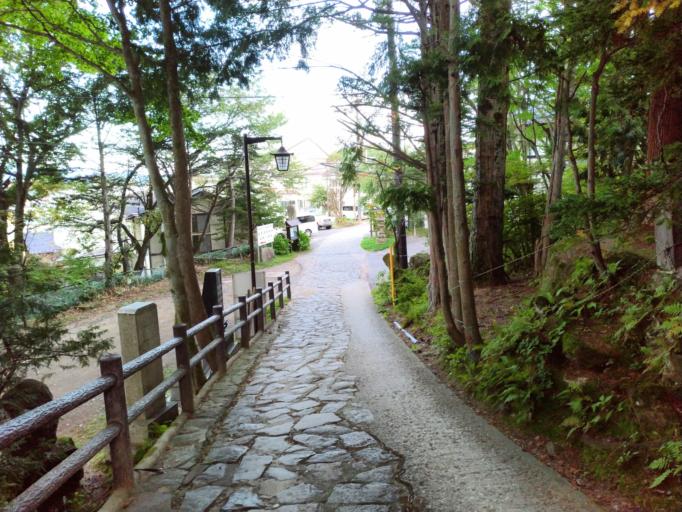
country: JP
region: Gunma
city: Nakanojomachi
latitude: 36.6218
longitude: 138.5958
